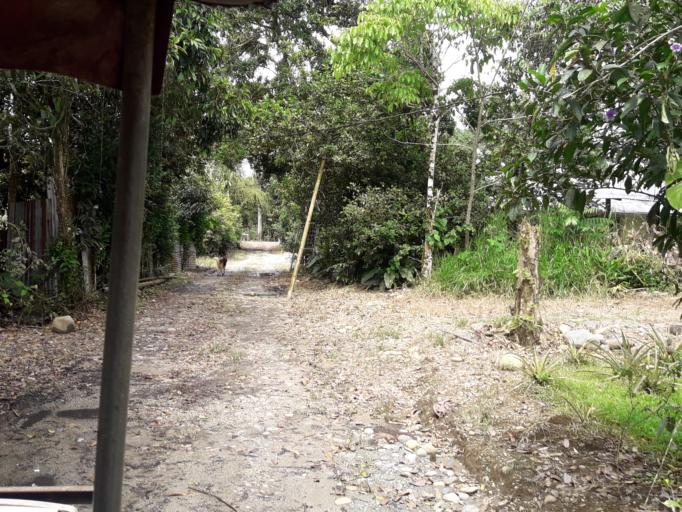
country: EC
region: Napo
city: Tena
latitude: -1.0723
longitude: -77.7957
